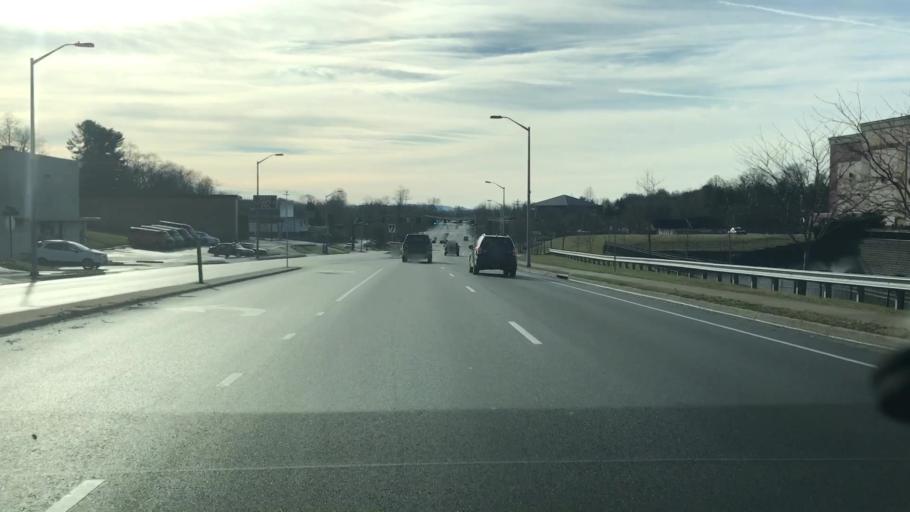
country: US
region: Virginia
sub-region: Montgomery County
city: Blacksburg
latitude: 37.2130
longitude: -80.4001
